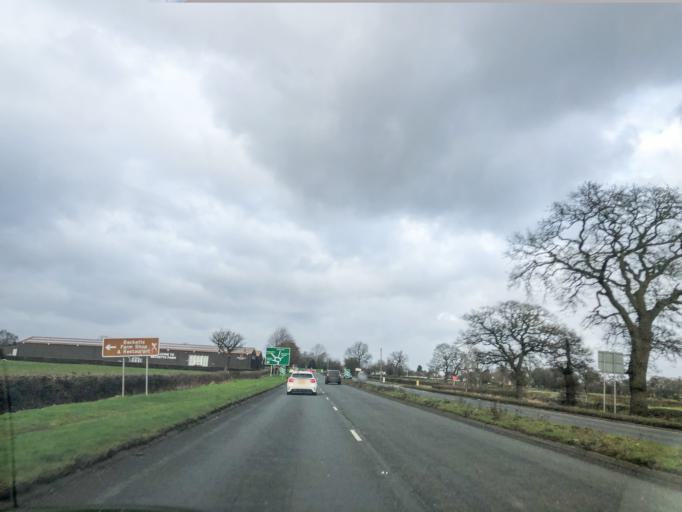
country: GB
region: England
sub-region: Solihull
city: Tidbury Green
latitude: 52.3700
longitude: -1.8872
